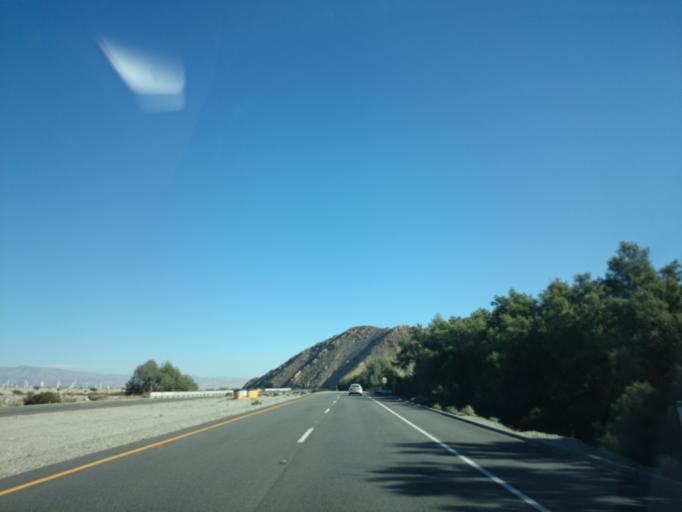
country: US
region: California
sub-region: Riverside County
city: Garnet
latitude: 33.9016
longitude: -116.6395
